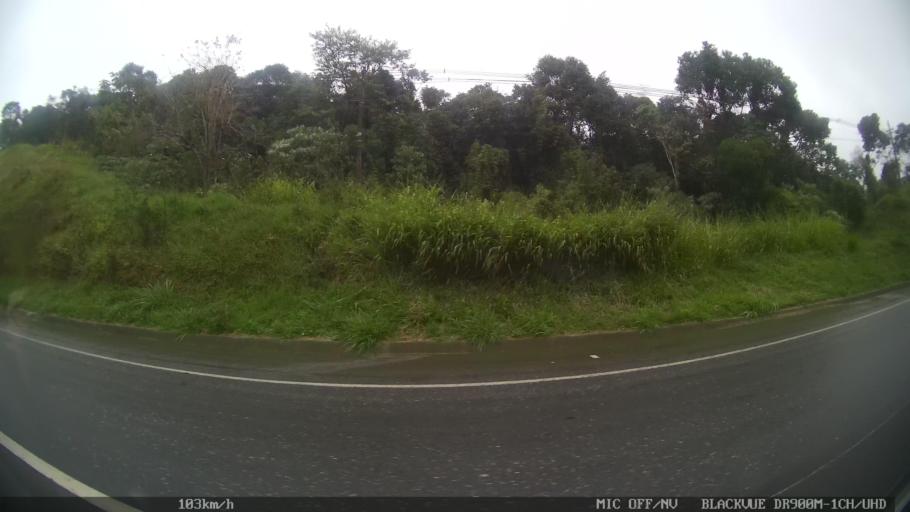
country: BR
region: Sao Paulo
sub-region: Juquitiba
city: Juquitiba
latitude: -23.9409
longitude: -47.0532
